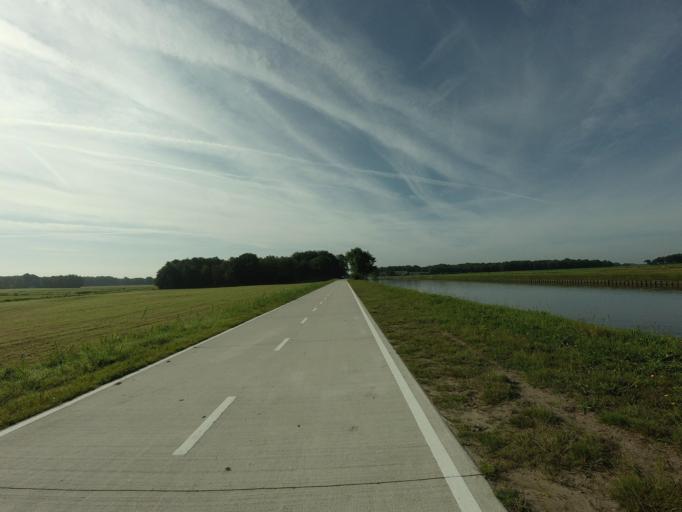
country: NL
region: Drenthe
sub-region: Gemeente Tynaarlo
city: Tynaarlo
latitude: 53.0453
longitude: 6.6085
